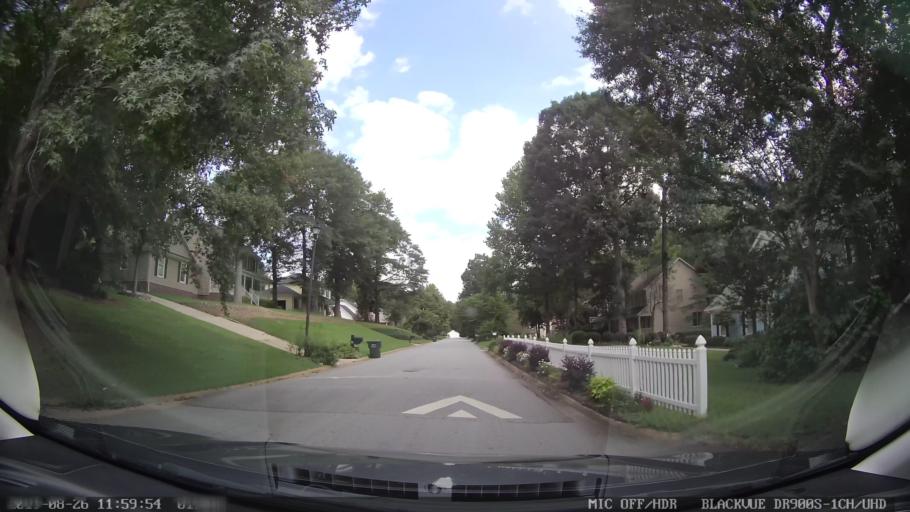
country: US
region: South Carolina
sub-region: Greenville County
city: Five Forks
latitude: 34.7981
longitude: -82.2348
